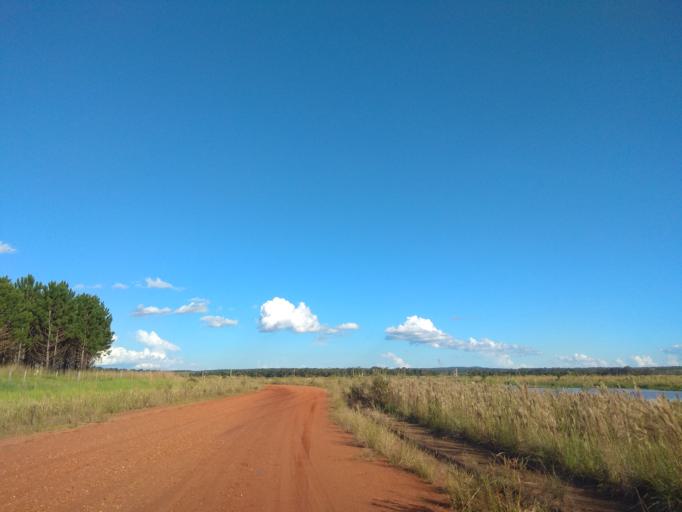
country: AR
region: Misiones
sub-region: Departamento de Candelaria
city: Candelaria
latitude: -27.4927
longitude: -55.7757
